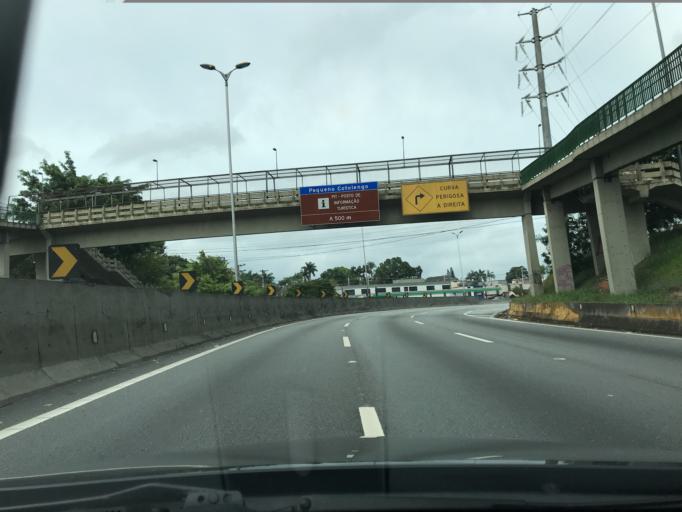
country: BR
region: Sao Paulo
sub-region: Embu
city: Embu
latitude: -23.5997
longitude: -46.8453
